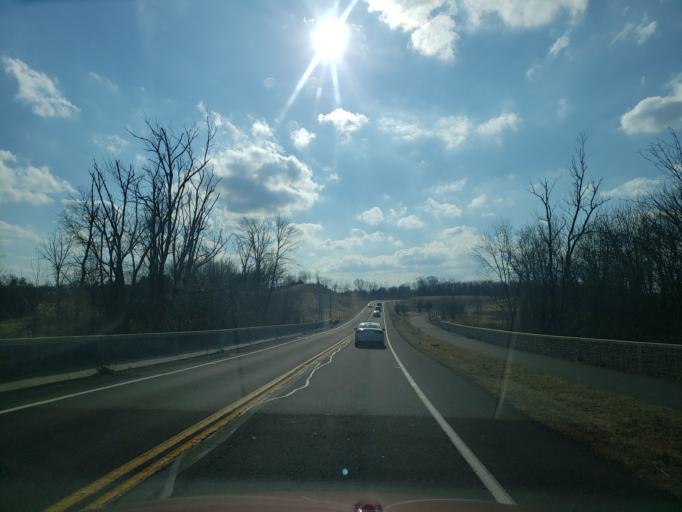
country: US
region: Pennsylvania
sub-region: Bucks County
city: New Britain
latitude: 40.2858
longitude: -75.1650
